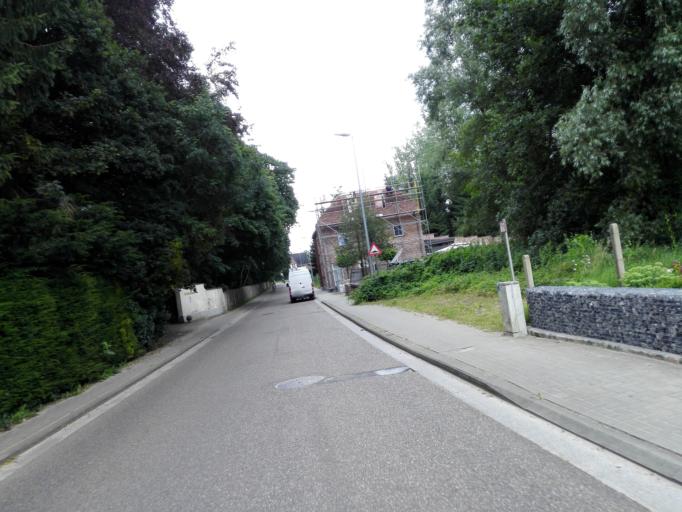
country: BE
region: Flanders
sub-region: Provincie Vlaams-Brabant
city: Bierbeek
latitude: 50.8590
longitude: 4.7621
